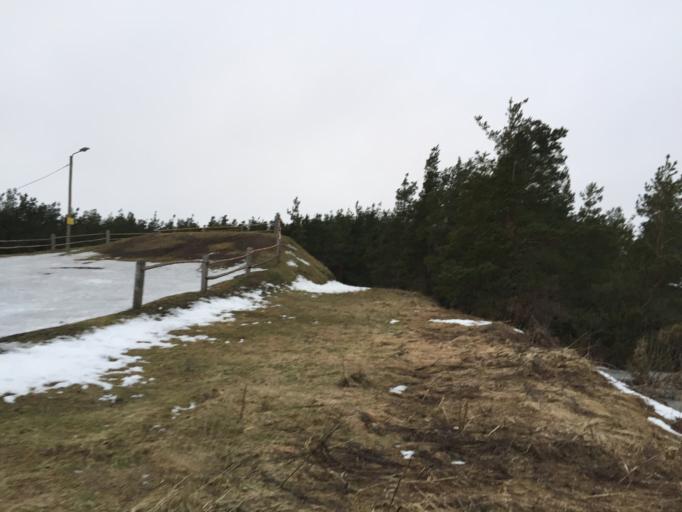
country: EE
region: Saare
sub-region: Kuressaare linn
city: Kuressaare
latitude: 58.2454
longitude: 22.5034
